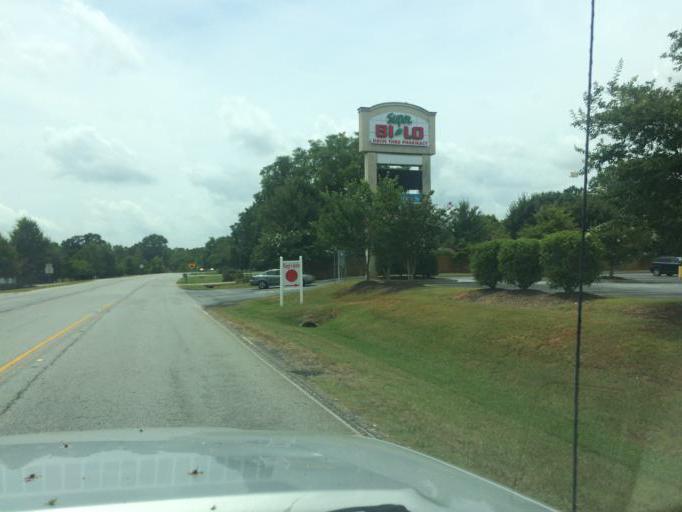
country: US
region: South Carolina
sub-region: Anderson County
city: Centerville
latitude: 34.5106
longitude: -82.7609
